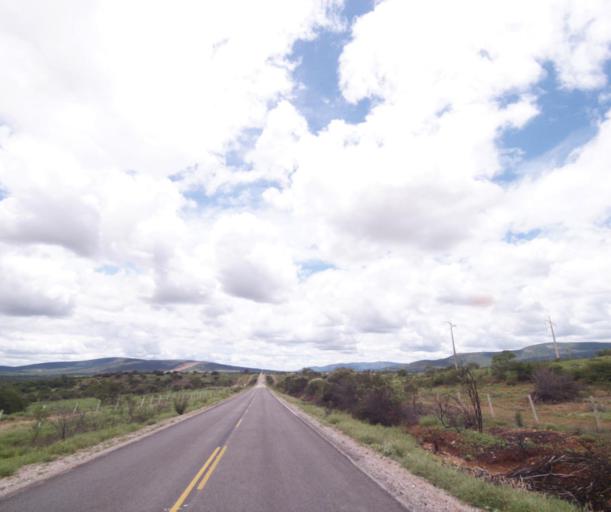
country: BR
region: Bahia
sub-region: Brumado
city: Brumado
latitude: -14.1557
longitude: -41.5181
